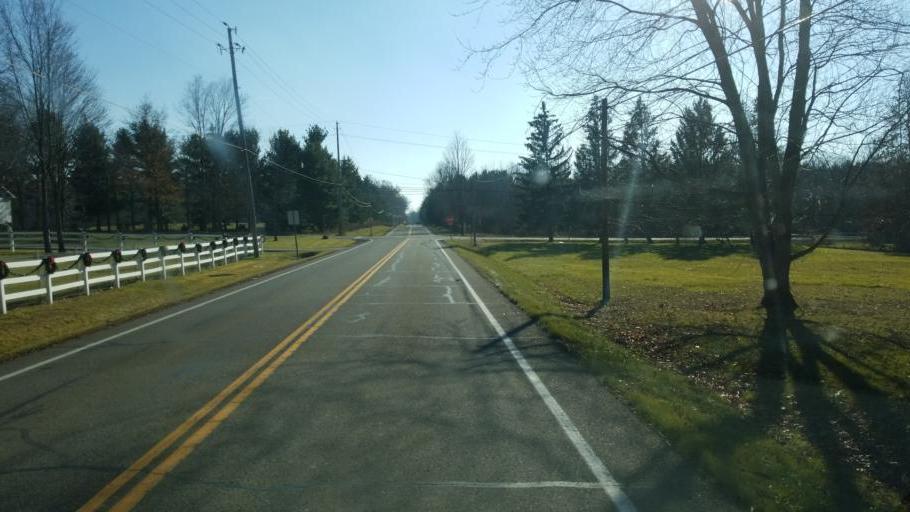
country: US
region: Ohio
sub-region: Geauga County
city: Bainbridge
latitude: 41.4338
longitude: -81.2482
